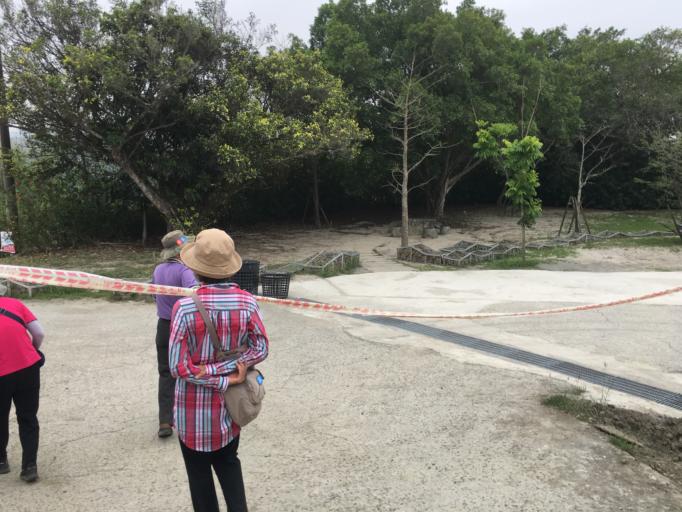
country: TW
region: Taiwan
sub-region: Tainan
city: Tainan
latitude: 22.8883
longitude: 120.3887
